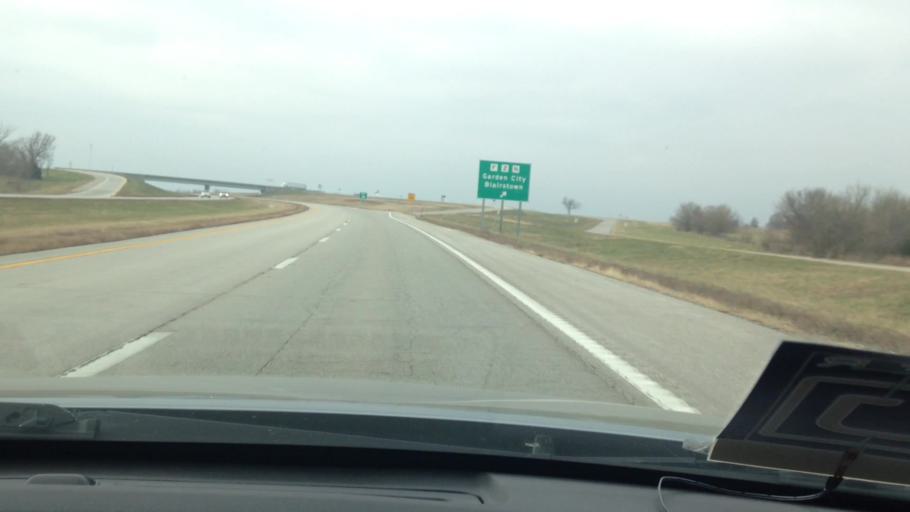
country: US
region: Missouri
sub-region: Cass County
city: Garden City
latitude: 38.5691
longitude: -94.1882
